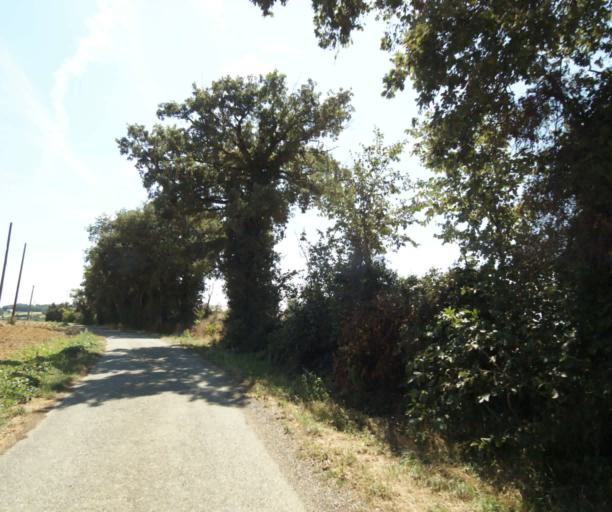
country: FR
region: Midi-Pyrenees
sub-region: Departement de l'Ariege
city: Lezat-sur-Leze
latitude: 43.2477
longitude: 1.3280
